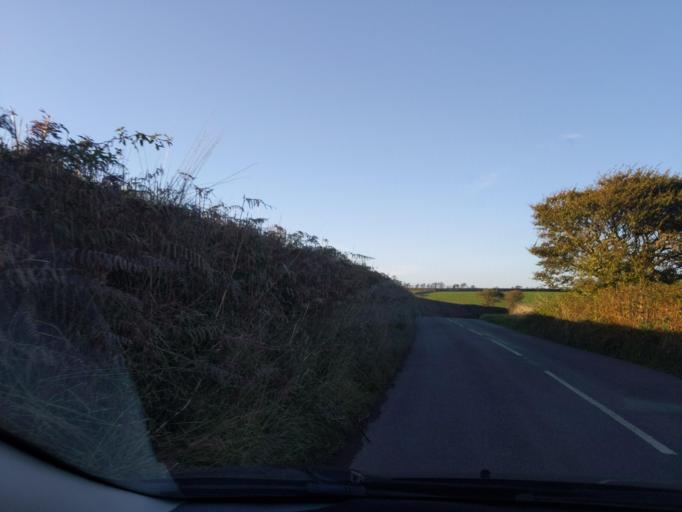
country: GB
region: England
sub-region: Plymouth
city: Plymstock
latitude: 50.3375
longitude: -4.0962
